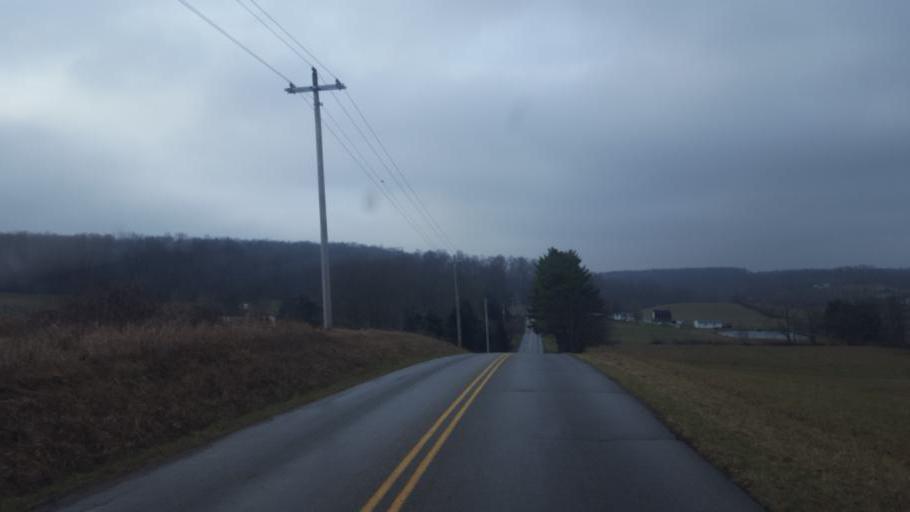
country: US
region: Ohio
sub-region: Knox County
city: Danville
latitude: 40.5154
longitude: -82.3619
